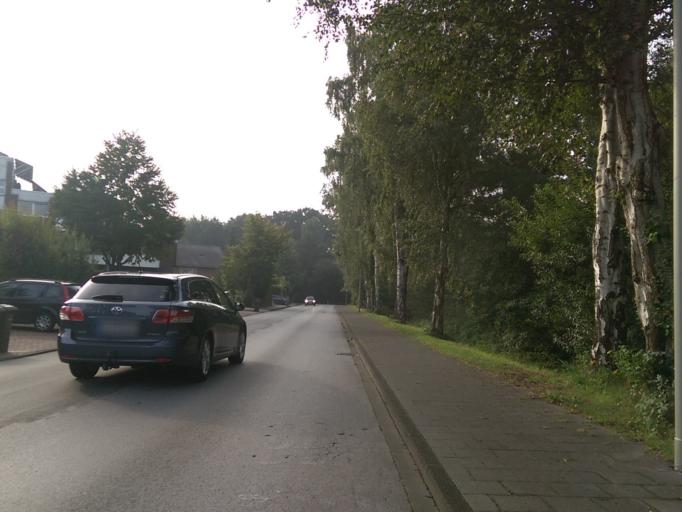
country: DE
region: North Rhine-Westphalia
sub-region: Regierungsbezirk Detmold
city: Harsewinkel
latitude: 51.9526
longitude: 8.2801
